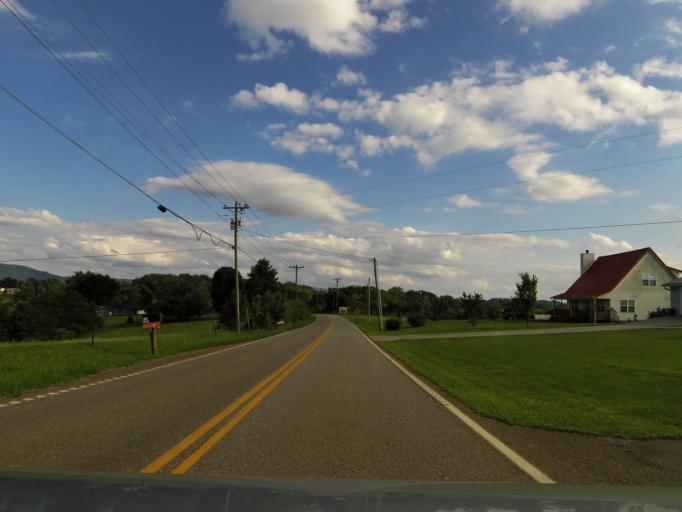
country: US
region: Tennessee
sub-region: Loudon County
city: Greenback
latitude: 35.6401
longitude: -84.1005
